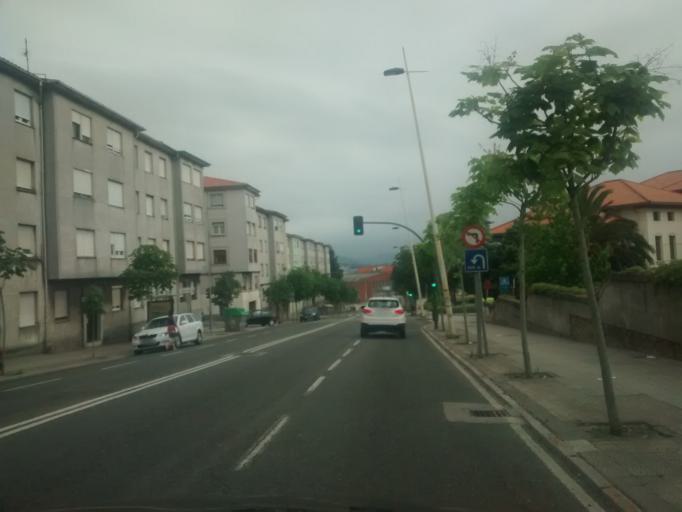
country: ES
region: Cantabria
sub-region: Provincia de Cantabria
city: Santander
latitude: 43.4563
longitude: -3.8271
